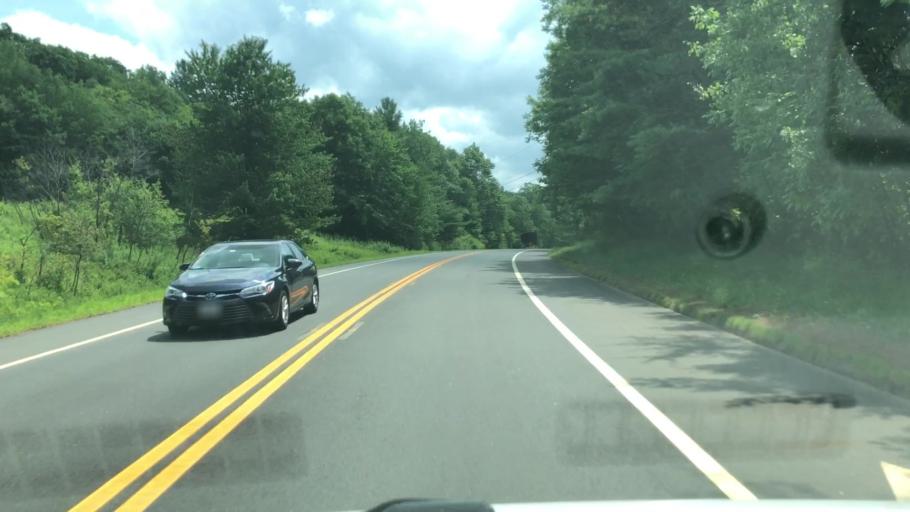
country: US
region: Massachusetts
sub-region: Franklin County
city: Ashfield
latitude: 42.5007
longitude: -72.8089
